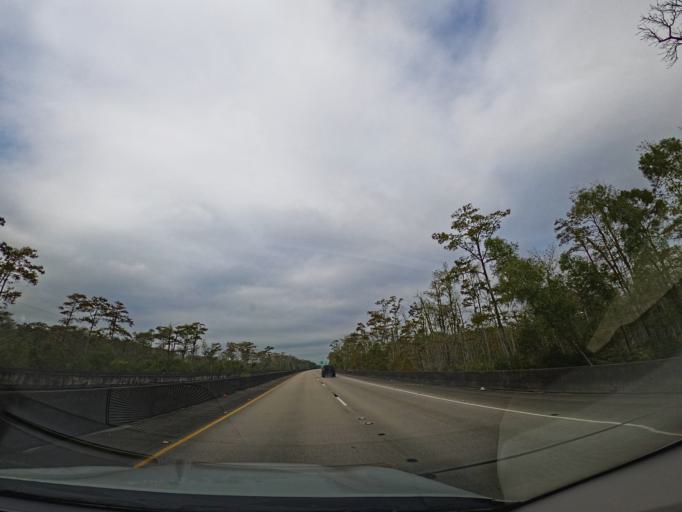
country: US
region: Louisiana
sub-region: Saint Mary Parish
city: Amelia
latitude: 29.6687
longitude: -91.0741
